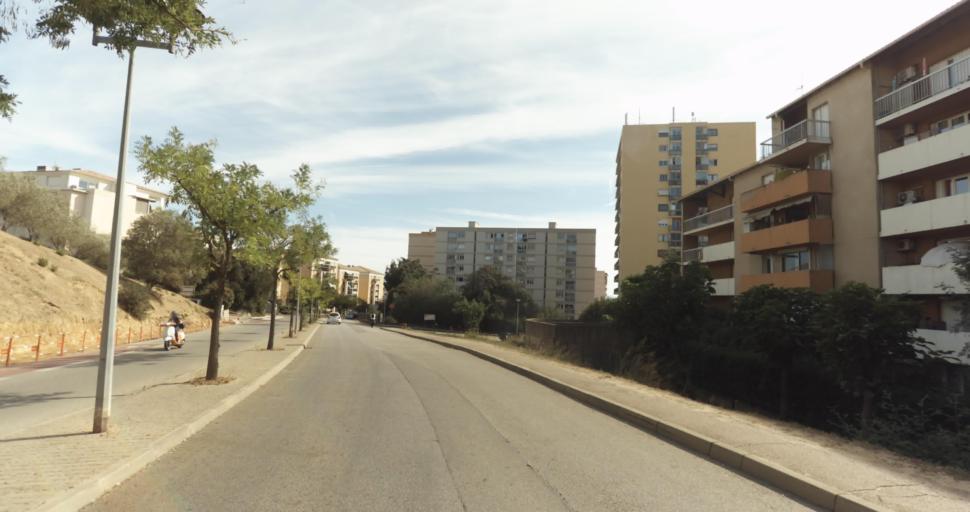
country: FR
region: Corsica
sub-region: Departement de la Corse-du-Sud
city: Ajaccio
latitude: 41.9412
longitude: 8.7500
